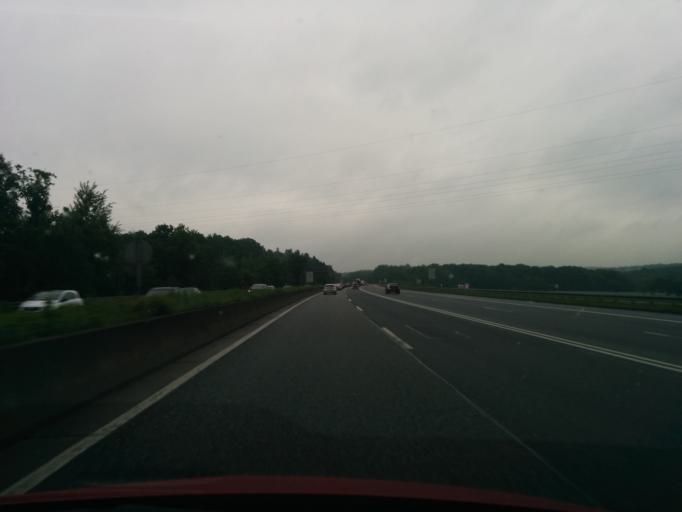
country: DE
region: Hesse
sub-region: Regierungsbezirk Kassel
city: Eichenzell
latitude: 50.4927
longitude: 9.7210
